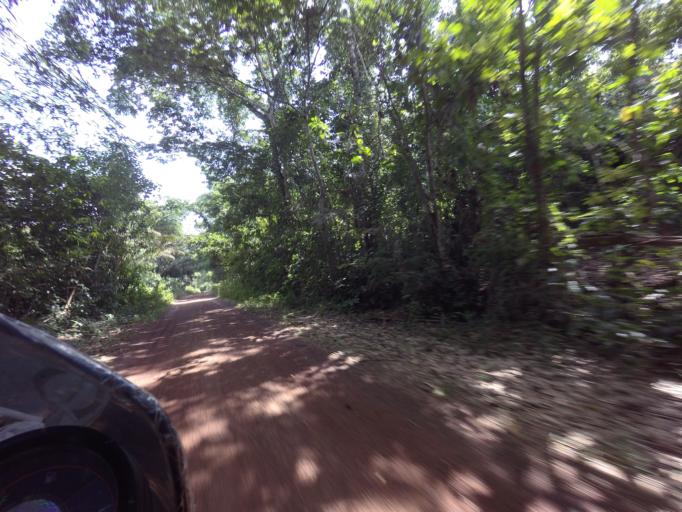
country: SL
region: Eastern Province
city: Daru
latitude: 8.0715
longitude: -10.8235
